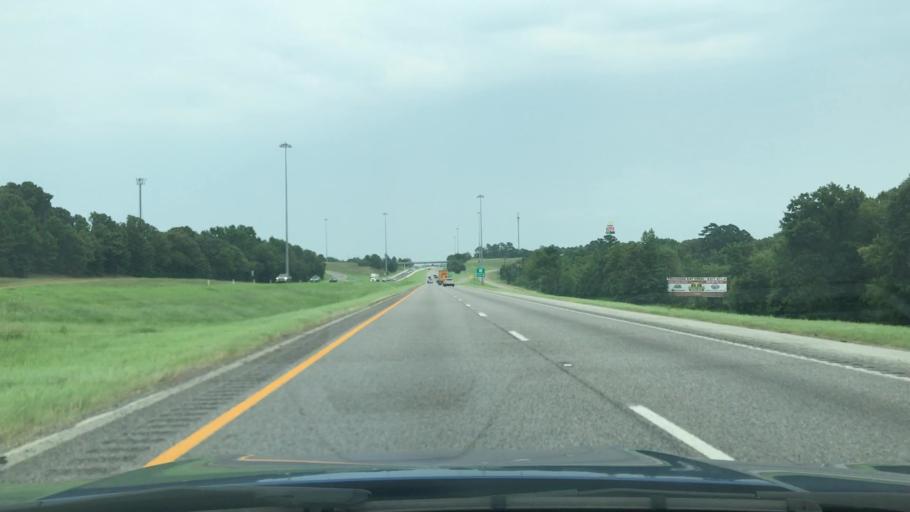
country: US
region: Texas
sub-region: Smith County
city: Tyler
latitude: 32.4543
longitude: -95.2922
